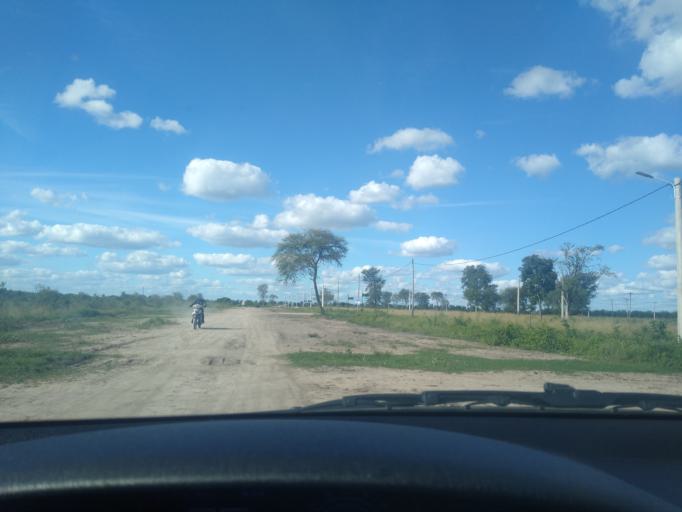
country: AR
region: Chaco
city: Resistencia
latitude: -27.4040
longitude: -58.9625
